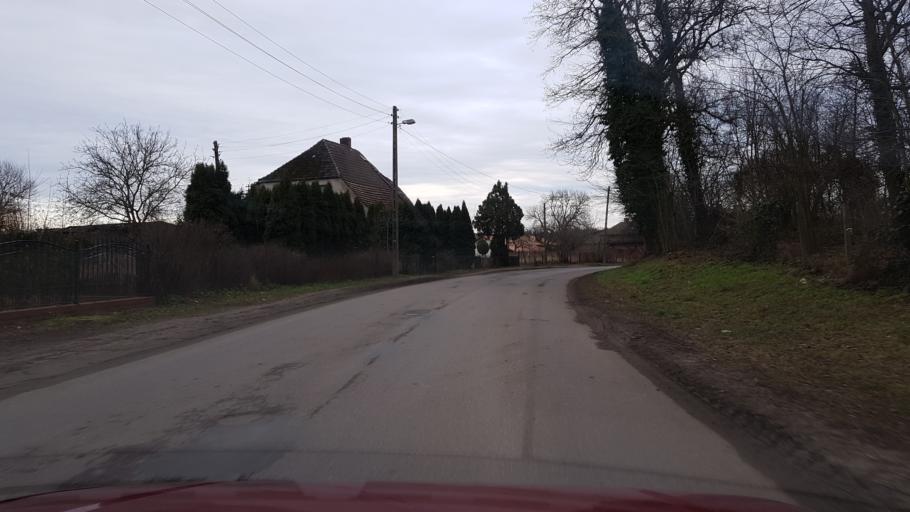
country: PL
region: West Pomeranian Voivodeship
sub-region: Powiat policki
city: Dobra
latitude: 53.5451
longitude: 14.4656
